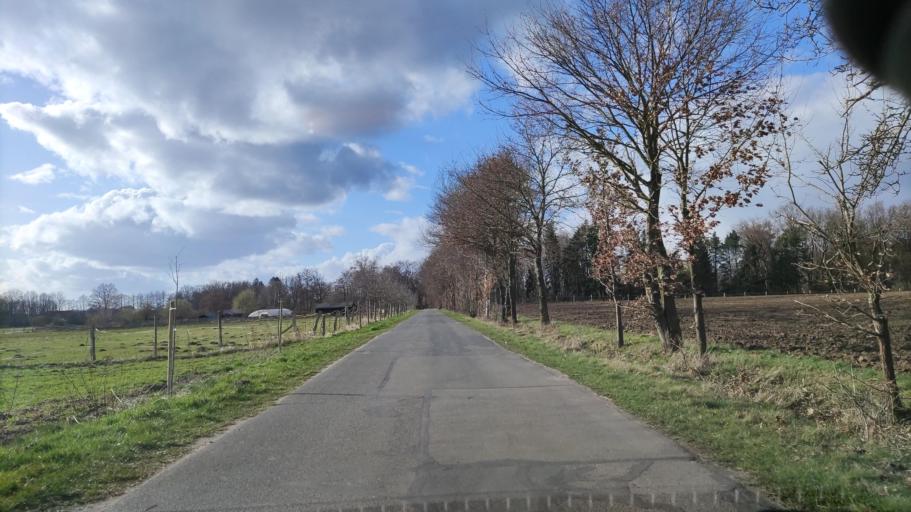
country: DE
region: Lower Saxony
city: Jelmstorf
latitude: 53.1293
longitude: 10.5172
